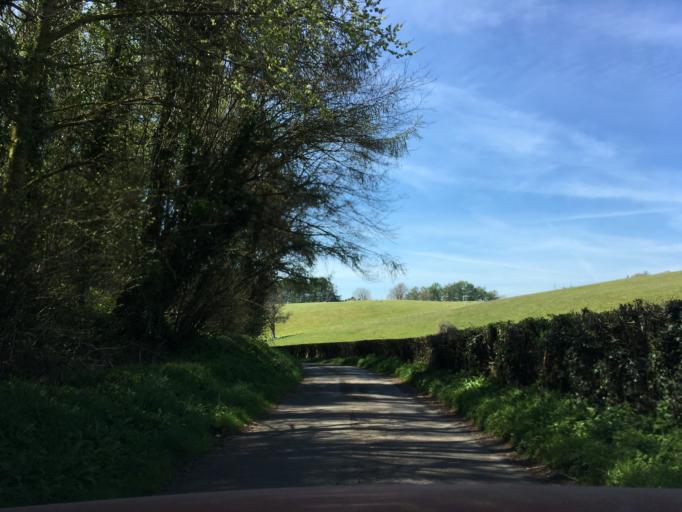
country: GB
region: Wales
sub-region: Monmouthshire
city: Chepstow
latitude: 51.6498
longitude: -2.7393
